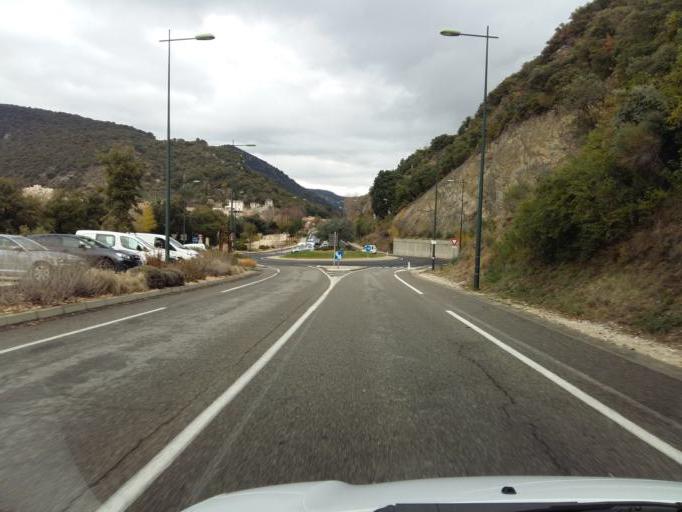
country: FR
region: Rhone-Alpes
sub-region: Departement de la Drome
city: Nyons
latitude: 44.3573
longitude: 5.1413
